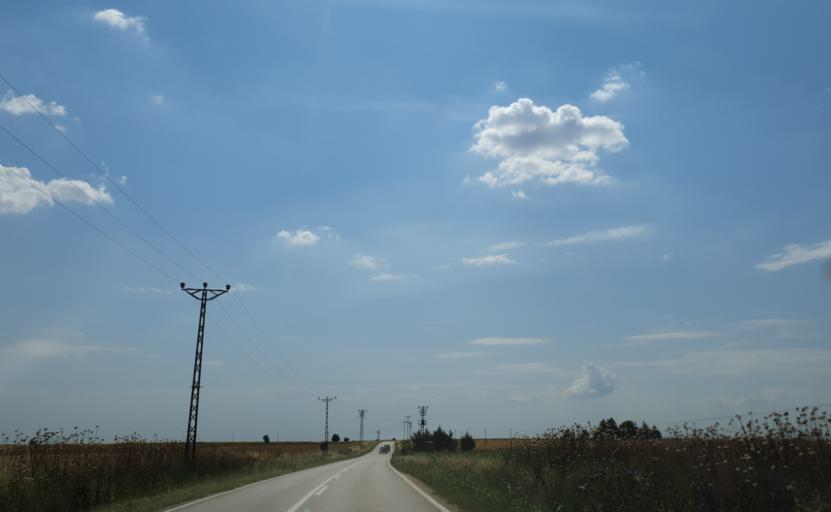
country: TR
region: Tekirdag
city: Beyazkoy
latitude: 41.4476
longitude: 27.6170
